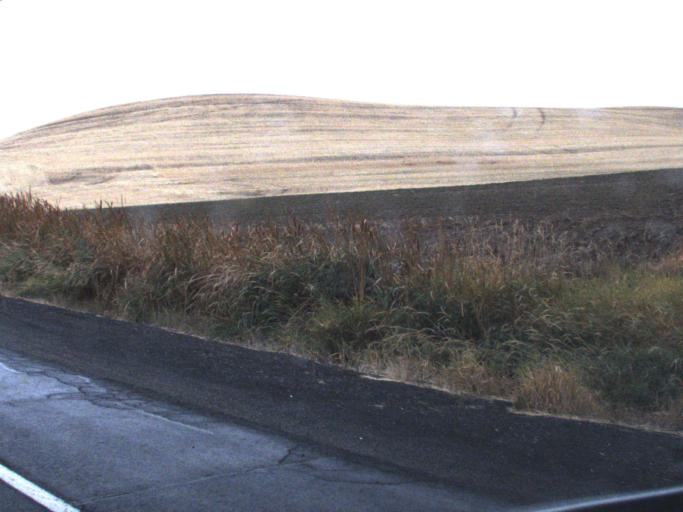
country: US
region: Washington
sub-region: Whitman County
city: Pullman
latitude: 46.7353
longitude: -117.2251
